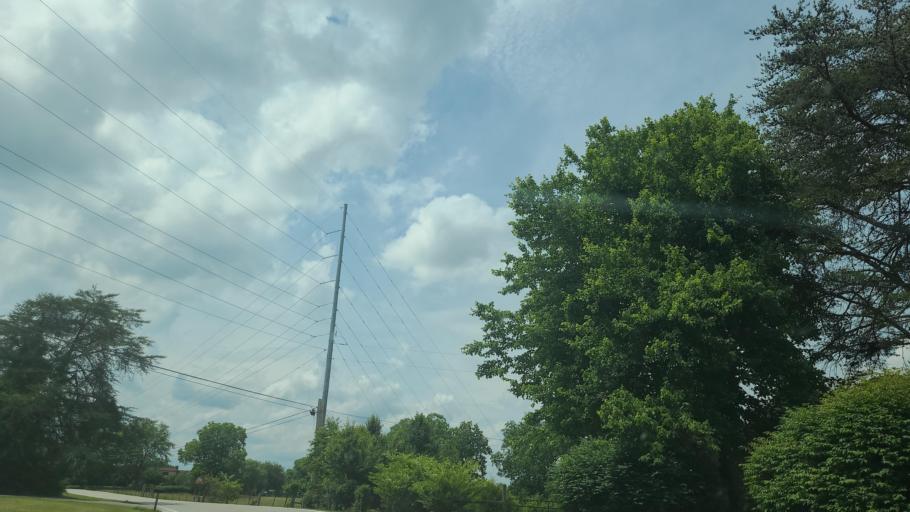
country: US
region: Tennessee
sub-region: Cumberland County
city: Crossville
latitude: 35.9049
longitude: -85.0027
